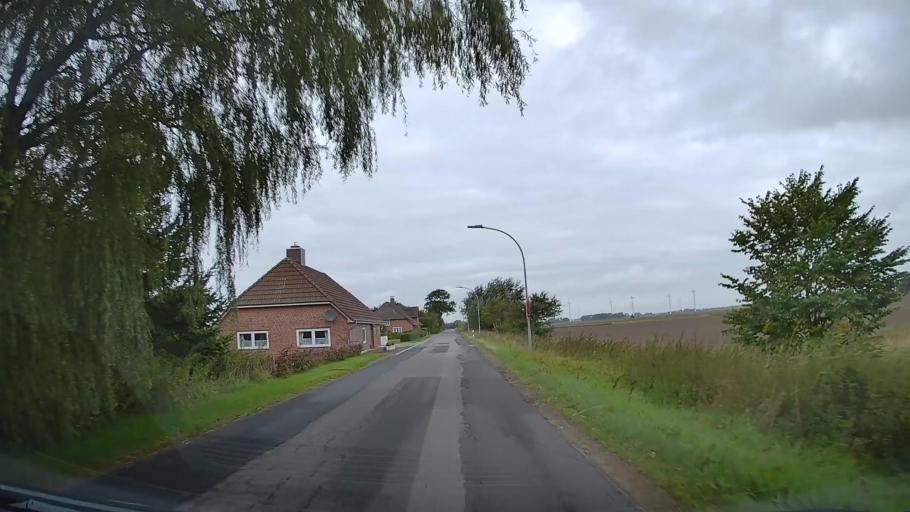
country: DE
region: Schleswig-Holstein
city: Galmsbull
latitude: 54.7767
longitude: 8.7322
